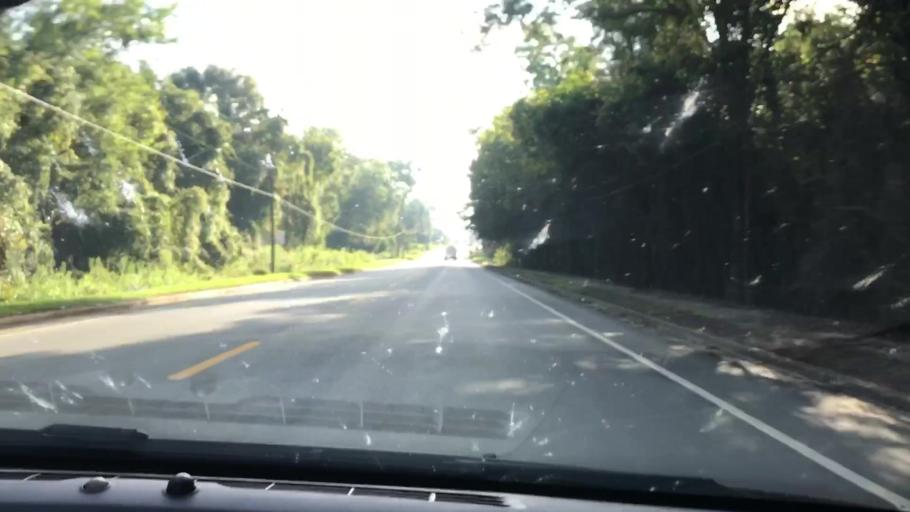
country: US
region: Georgia
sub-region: Terrell County
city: Dawson
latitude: 31.7699
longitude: -84.4541
